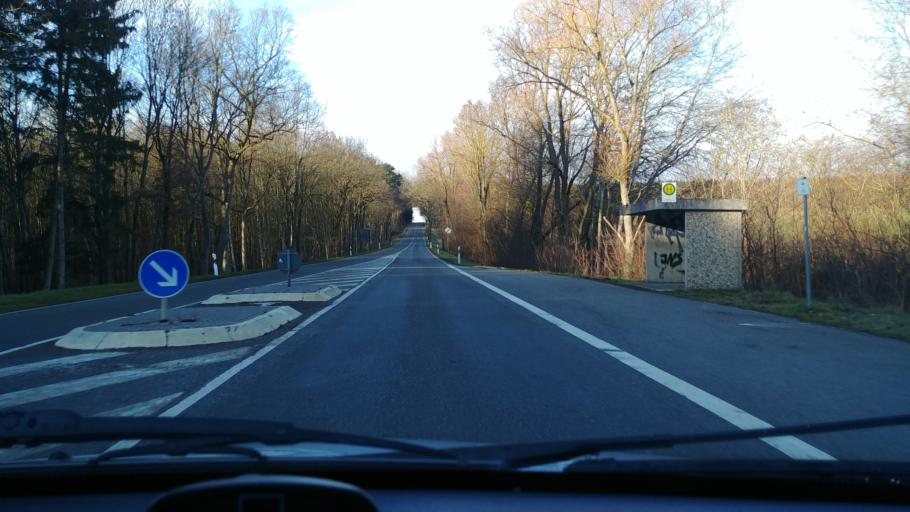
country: DE
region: Rheinland-Pfalz
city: Obertiefenbach
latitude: 50.2376
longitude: 7.8826
